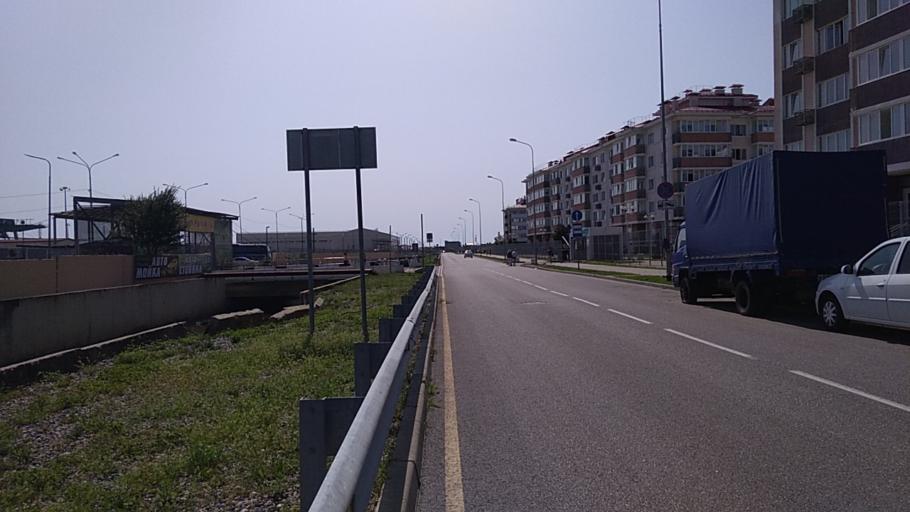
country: RU
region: Krasnodarskiy
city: Vysokoye
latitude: 43.4028
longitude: 39.9869
